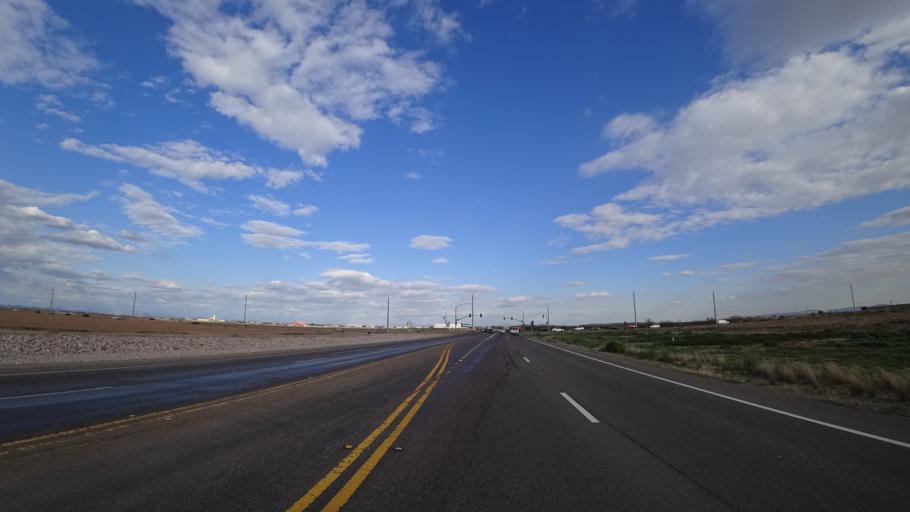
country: US
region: Arizona
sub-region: Maricopa County
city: Youngtown
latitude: 33.5511
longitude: -112.3434
